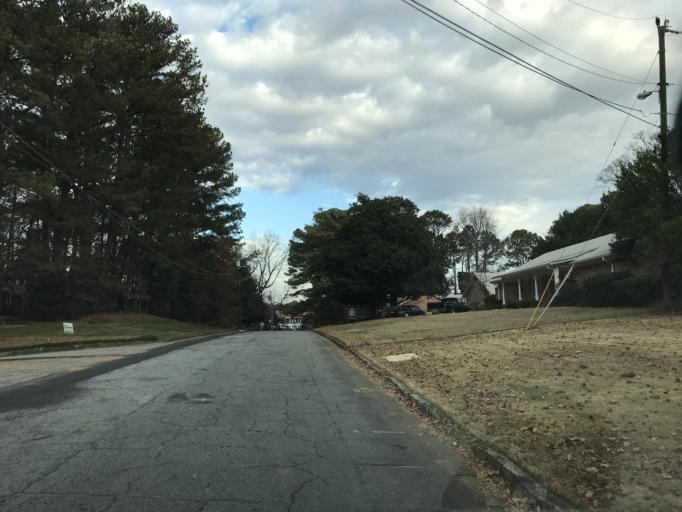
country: US
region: Georgia
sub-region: DeKalb County
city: Doraville
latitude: 33.8839
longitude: -84.2528
